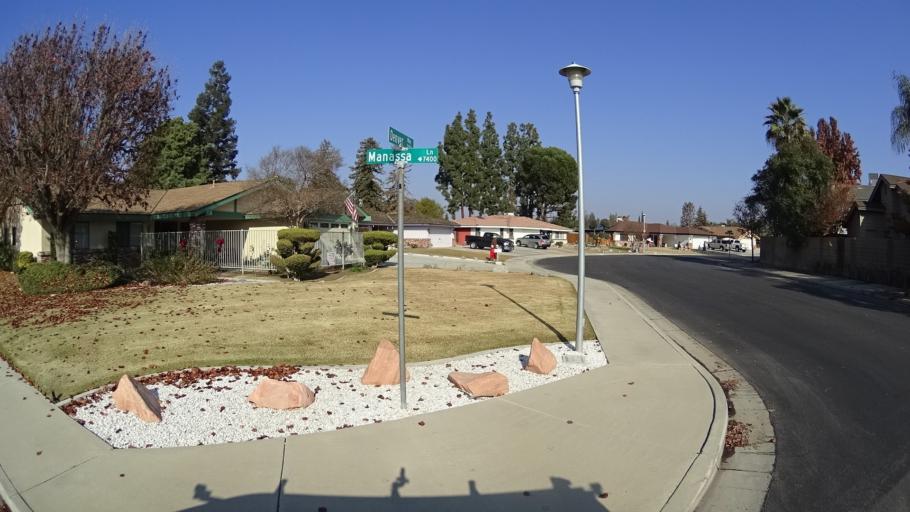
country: US
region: California
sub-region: Kern County
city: Greenacres
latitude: 35.3244
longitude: -119.0839
